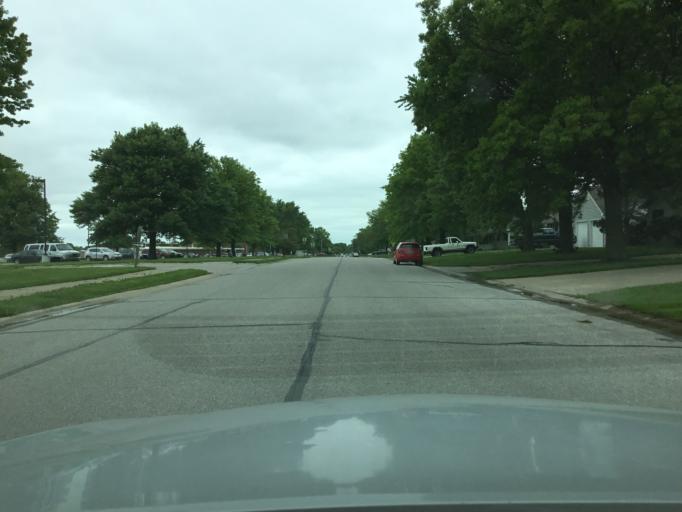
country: US
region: Kansas
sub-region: Franklin County
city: Ottawa
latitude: 38.5948
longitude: -95.2770
